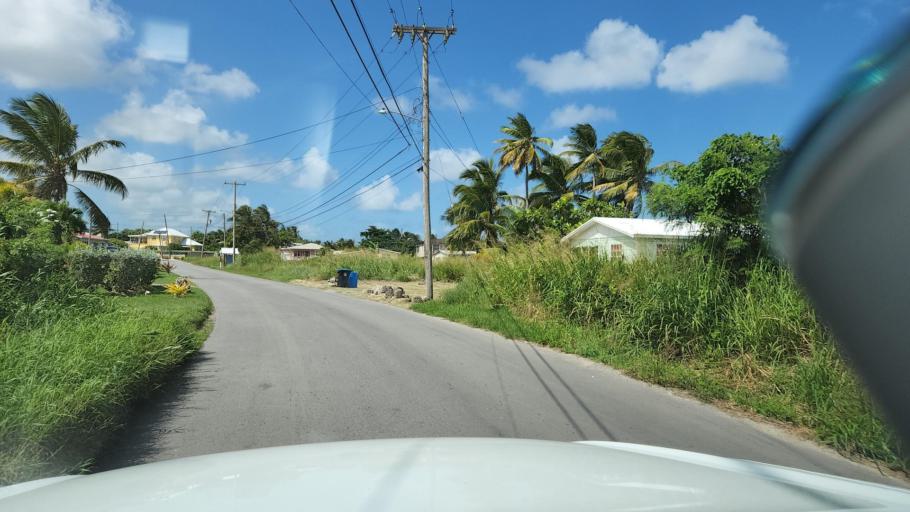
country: BB
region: Saint Philip
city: Crane
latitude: 13.1643
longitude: -59.4516
